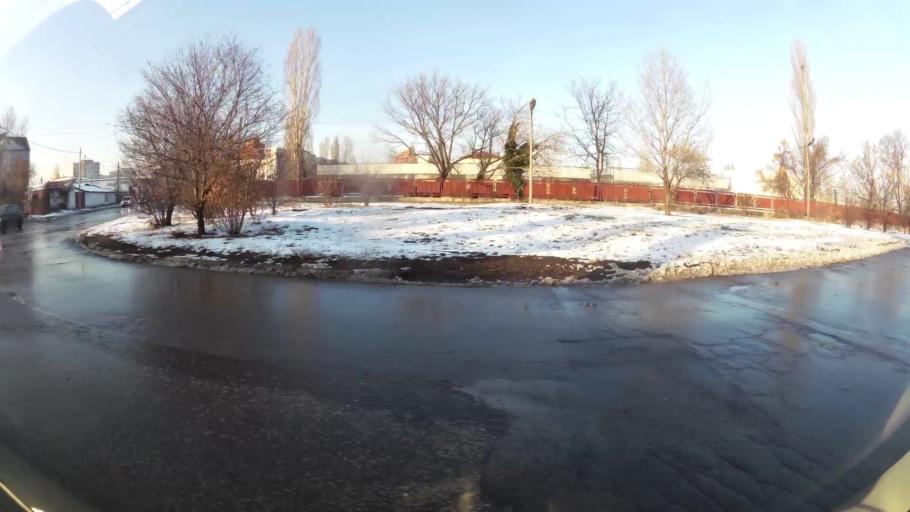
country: BG
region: Sofia-Capital
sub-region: Stolichna Obshtina
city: Sofia
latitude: 42.6760
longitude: 23.3803
